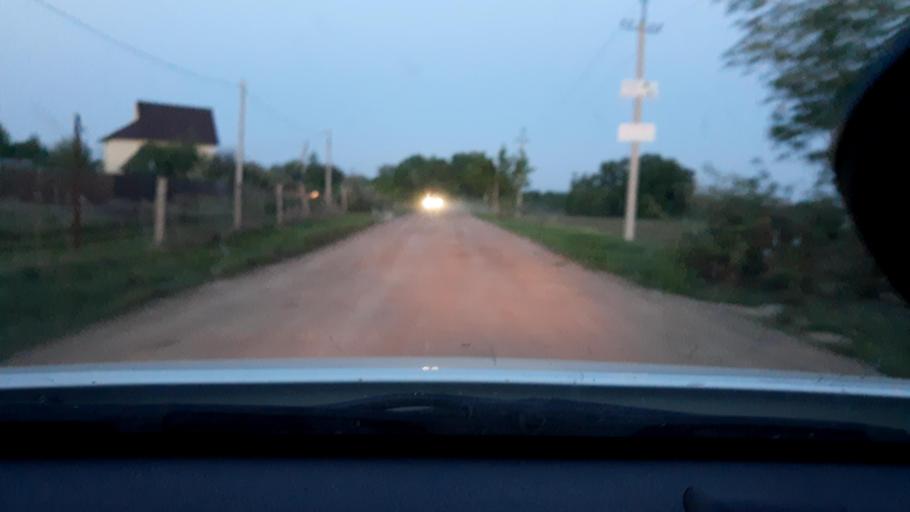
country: RU
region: Bashkortostan
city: Avdon
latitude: 54.5265
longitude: 55.8227
